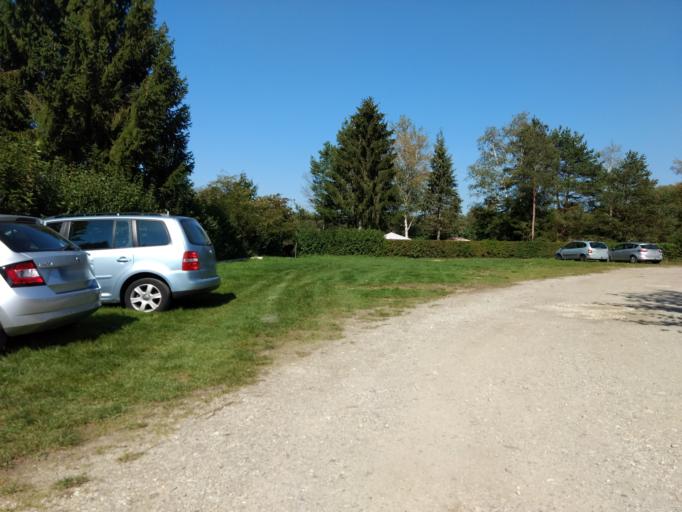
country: DE
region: Bavaria
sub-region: Upper Bavaria
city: Konigsdorf
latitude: 47.8332
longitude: 11.4737
